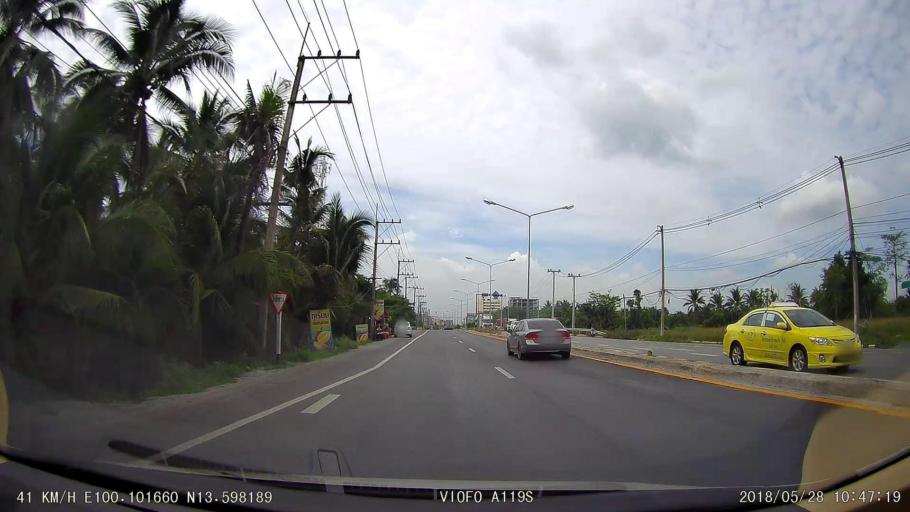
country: TH
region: Samut Sakhon
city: Ban Phaeo
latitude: 13.5981
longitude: 100.1017
